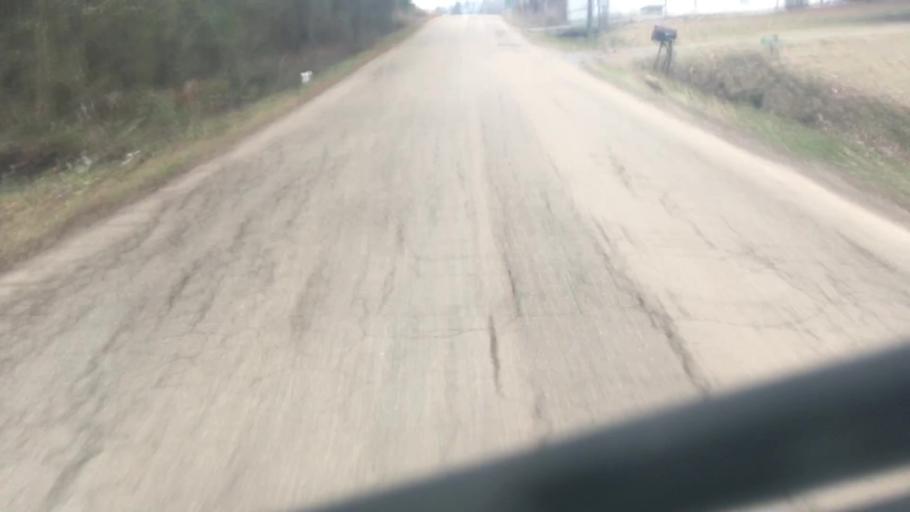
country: US
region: Alabama
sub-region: Walker County
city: Jasper
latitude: 33.8336
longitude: -87.2254
